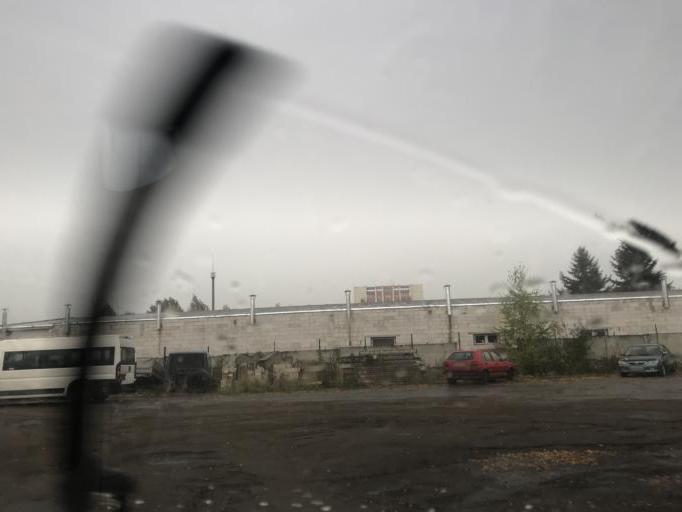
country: BY
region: Mogilev
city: Buynichy
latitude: 53.8928
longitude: 30.2960
